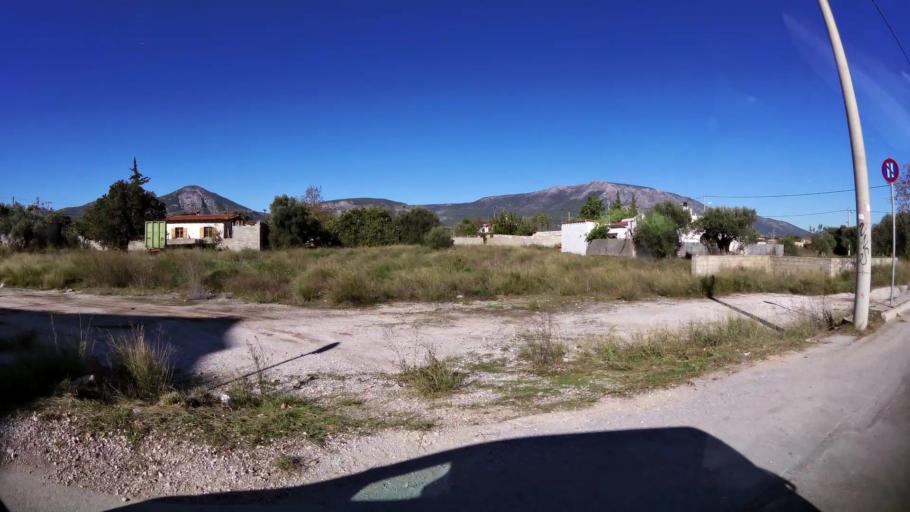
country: GR
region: Attica
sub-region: Nomarchia Anatolikis Attikis
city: Koropi
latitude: 37.9062
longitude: 23.8683
